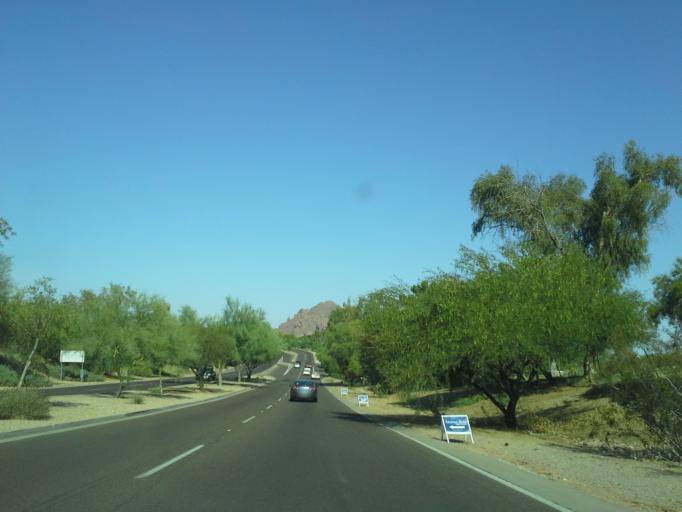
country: US
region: Arizona
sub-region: Maricopa County
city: Paradise Valley
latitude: 33.5303
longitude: -112.0235
